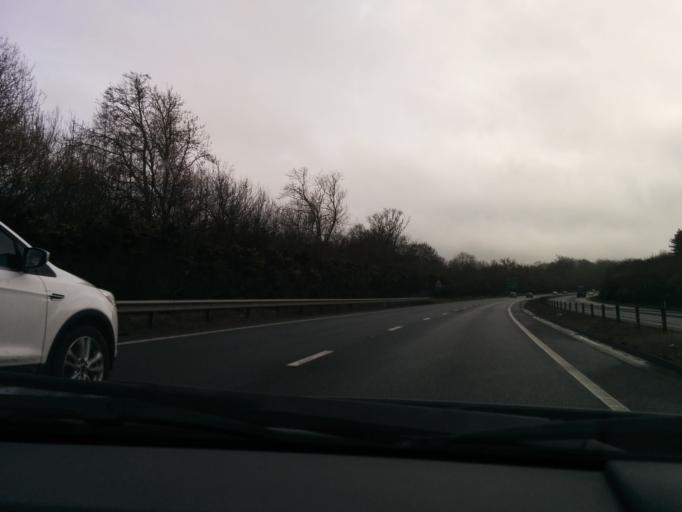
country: GB
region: England
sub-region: Hampshire
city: Highclere
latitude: 51.3589
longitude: -1.3473
